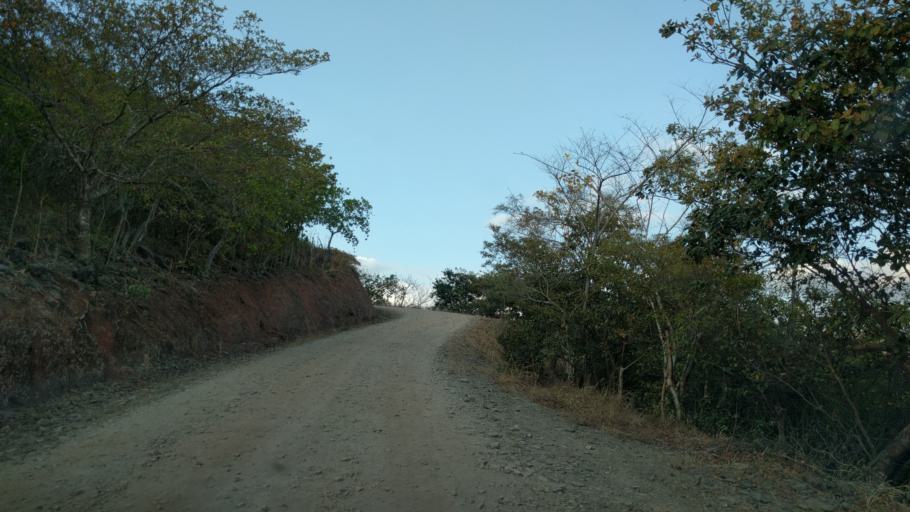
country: CR
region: Puntarenas
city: Esparza
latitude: 10.0214
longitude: -84.6986
